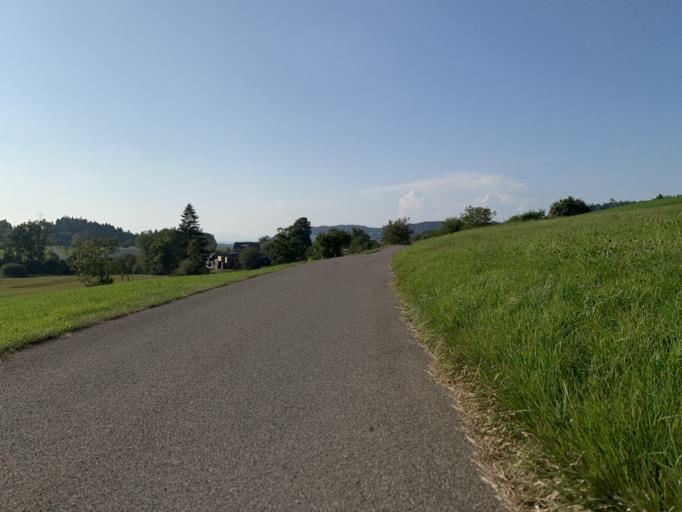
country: CH
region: Zurich
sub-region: Bezirk Hinwil
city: Baretswil
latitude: 47.3239
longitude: 8.8759
